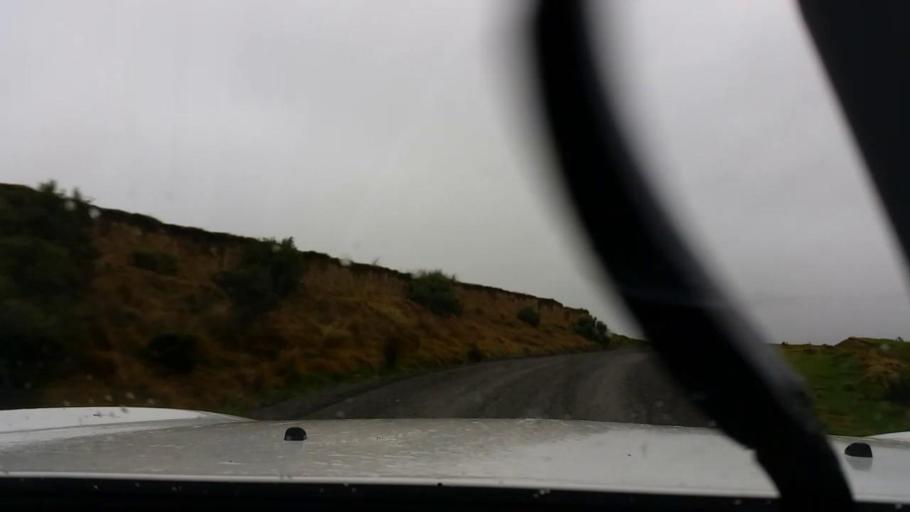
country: NZ
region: Wellington
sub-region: Masterton District
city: Masterton
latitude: -41.2500
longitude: 175.9026
